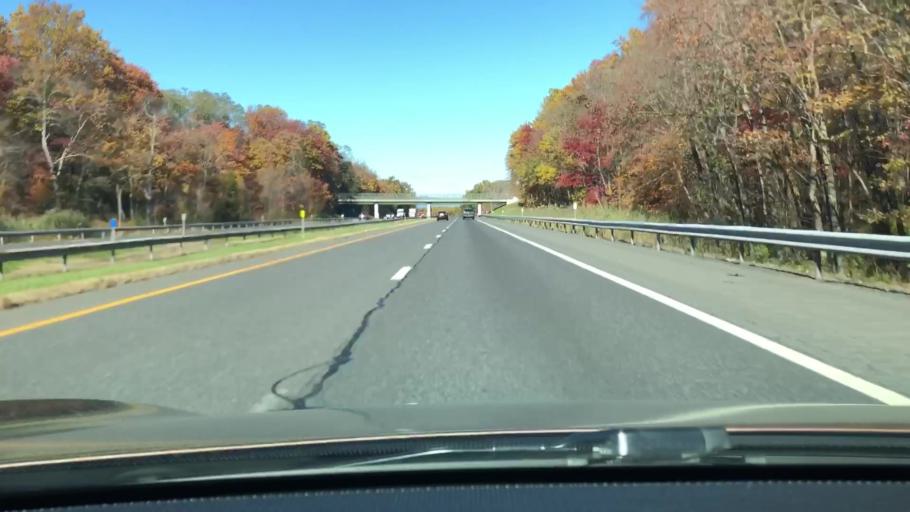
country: US
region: New York
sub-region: Ulster County
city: Tillson
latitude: 41.8285
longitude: -74.0573
